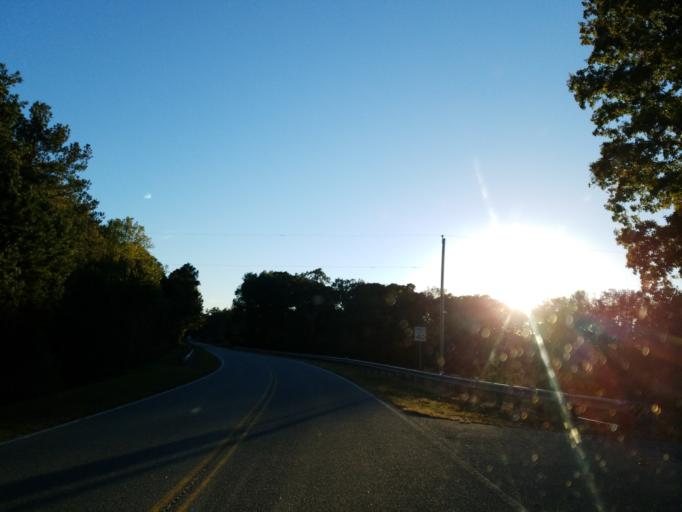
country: US
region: Georgia
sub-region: Forsyth County
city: Cumming
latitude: 34.2817
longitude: -84.0779
